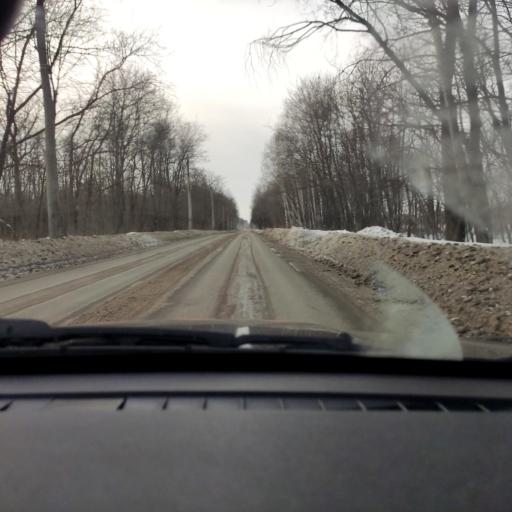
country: RU
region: Samara
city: Pribrezhnyy
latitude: 53.5156
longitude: 49.8489
